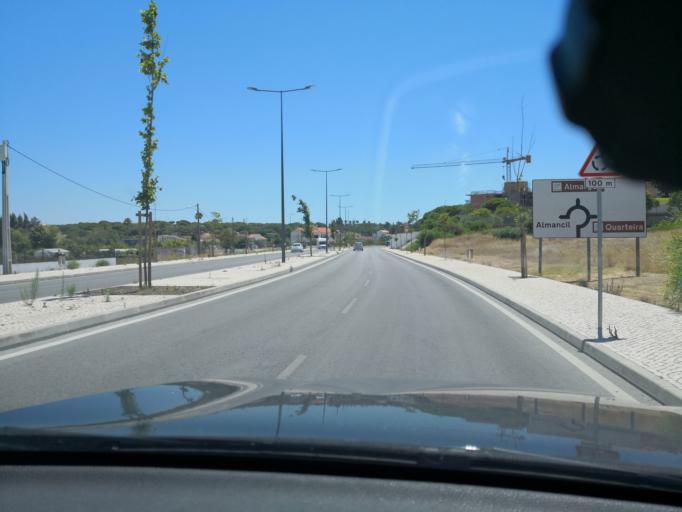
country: PT
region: Faro
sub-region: Loule
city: Quarteira
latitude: 37.0710
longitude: -8.0864
